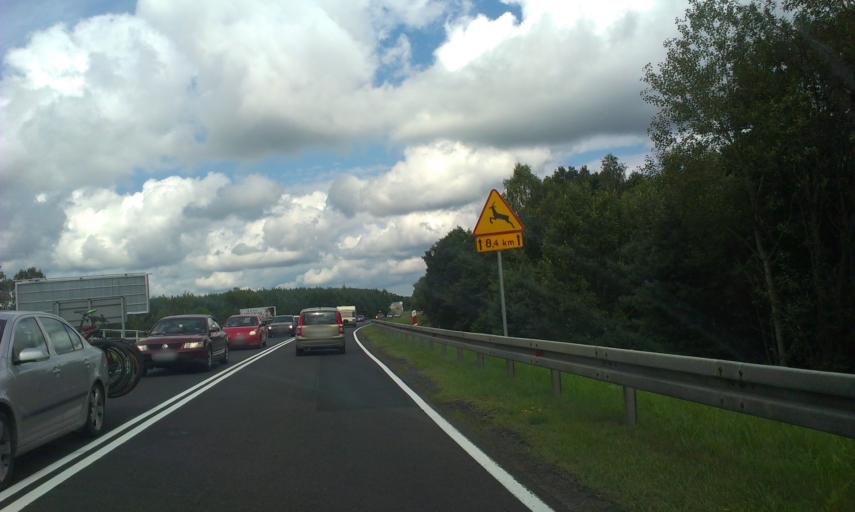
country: PL
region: West Pomeranian Voivodeship
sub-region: Powiat koszalinski
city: Bobolice
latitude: 53.9743
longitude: 16.5521
